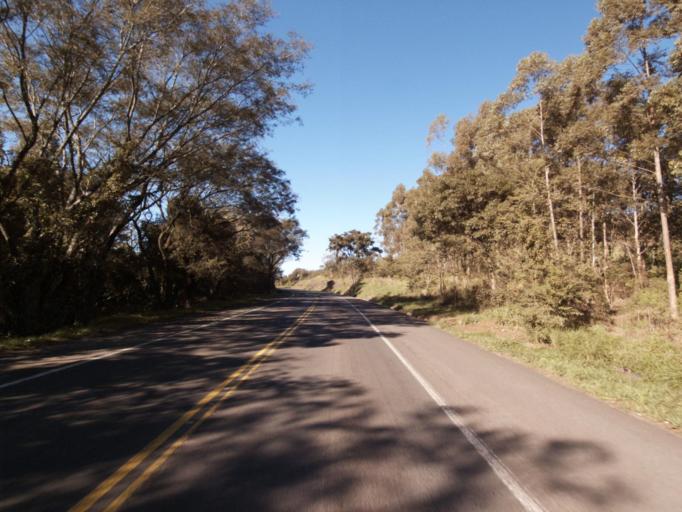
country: BR
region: Rio Grande do Sul
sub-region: Frederico Westphalen
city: Frederico Westphalen
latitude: -26.7974
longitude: -53.4496
